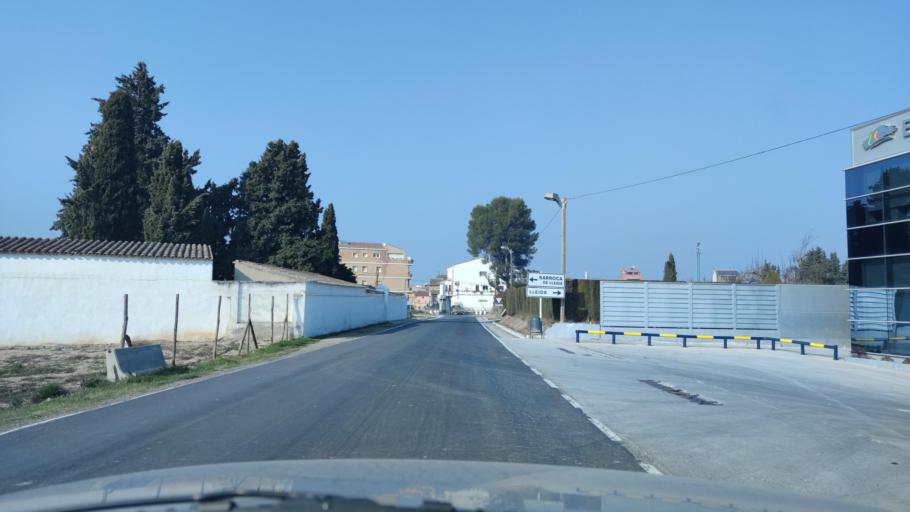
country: ES
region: Catalonia
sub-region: Provincia de Lleida
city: Lleida
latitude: 41.5719
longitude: 0.6079
